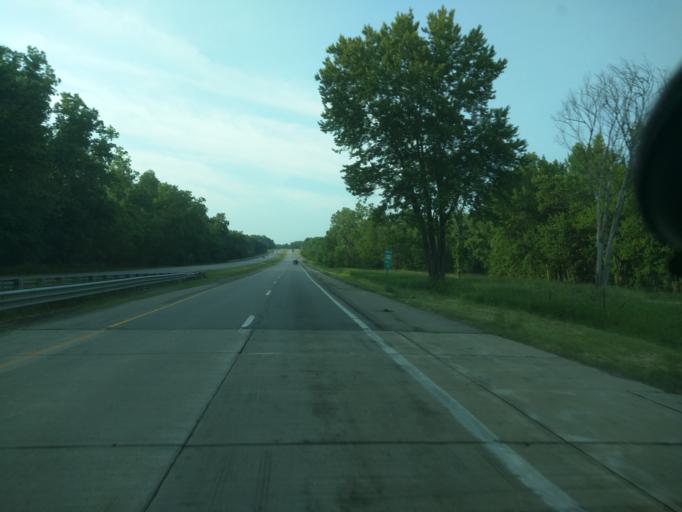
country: US
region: Michigan
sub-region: Ingham County
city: Leslie
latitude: 42.4026
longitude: -84.4290
